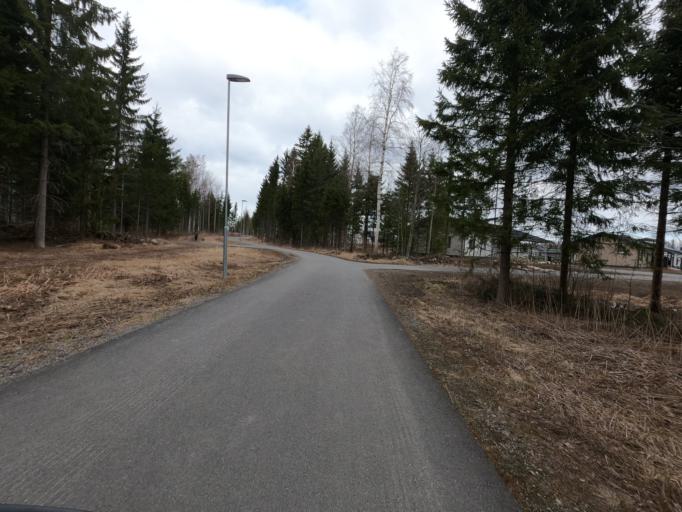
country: FI
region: North Karelia
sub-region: Joensuu
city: Joensuu
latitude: 62.5627
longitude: 29.8217
